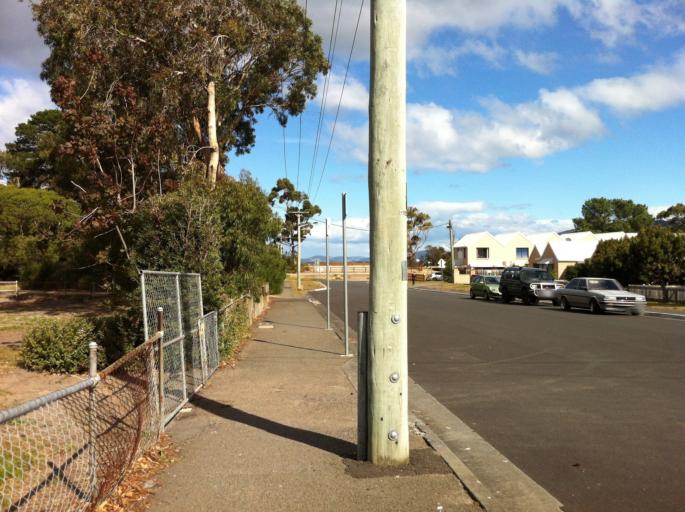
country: AU
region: Tasmania
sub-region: Clarence
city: Bellerive
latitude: -42.8776
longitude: 147.3827
